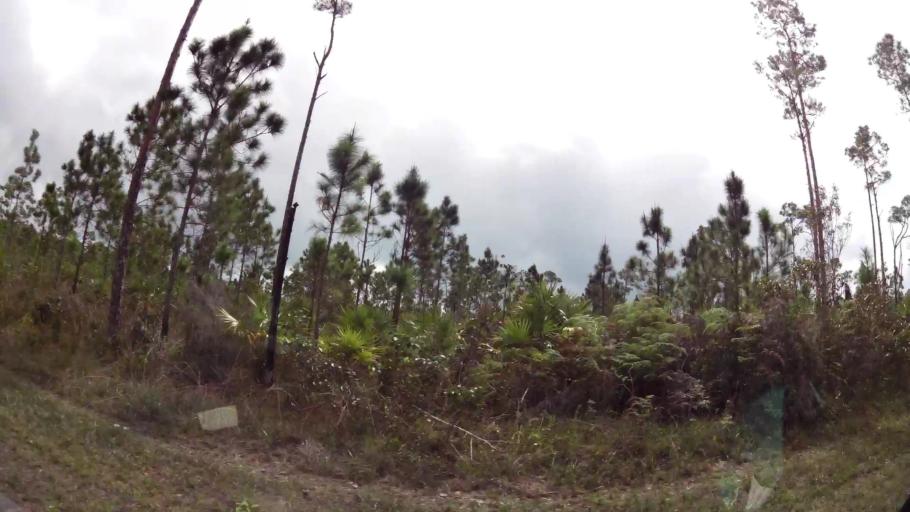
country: BS
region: Freeport
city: Lucaya
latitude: 26.5508
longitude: -78.5801
